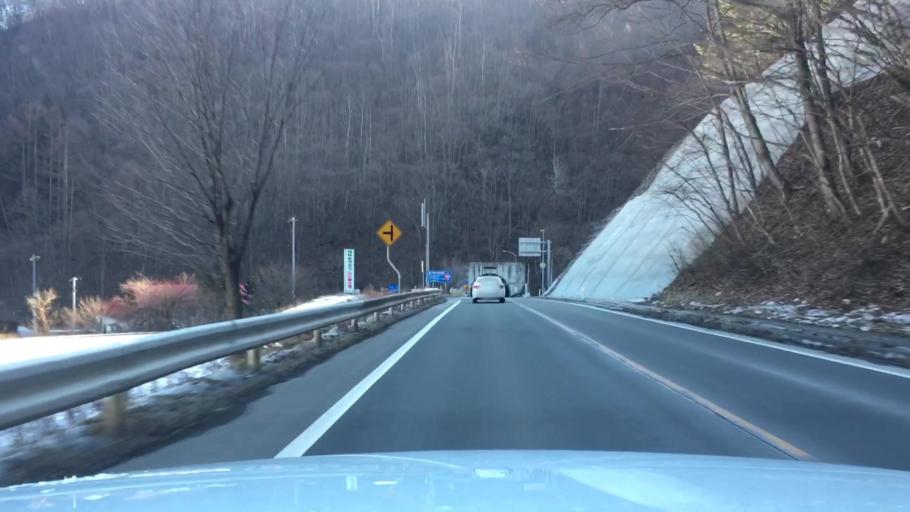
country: JP
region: Iwate
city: Tono
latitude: 39.6227
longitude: 141.6138
